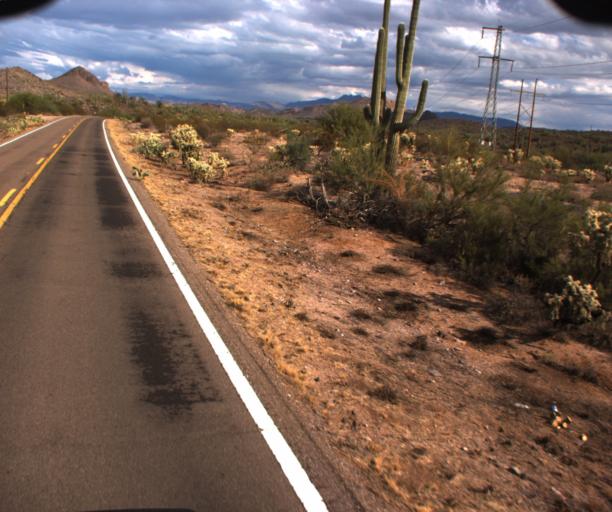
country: US
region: Arizona
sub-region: Pinal County
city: Apache Junction
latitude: 33.4765
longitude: -111.4752
